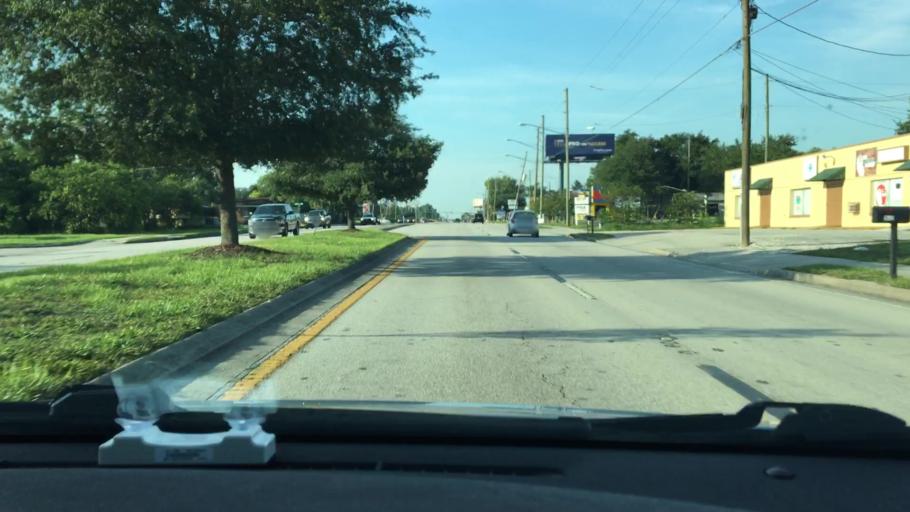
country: US
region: Florida
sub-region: Orange County
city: Union Park
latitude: 28.5734
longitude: -81.2862
